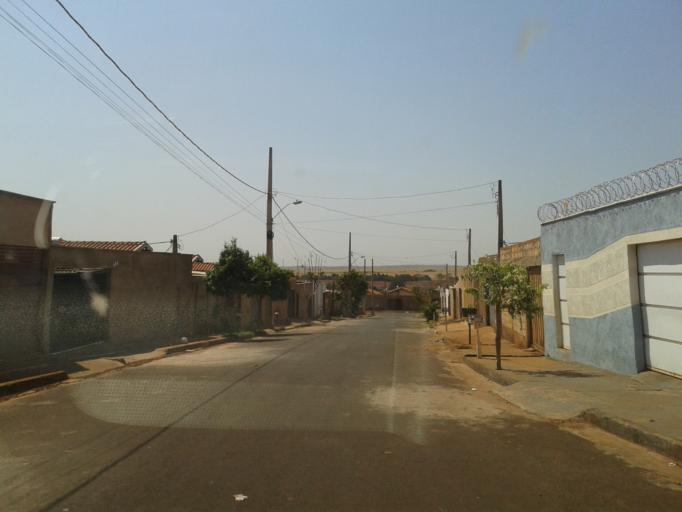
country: BR
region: Minas Gerais
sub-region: Ituiutaba
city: Ituiutaba
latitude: -19.0164
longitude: -49.4539
